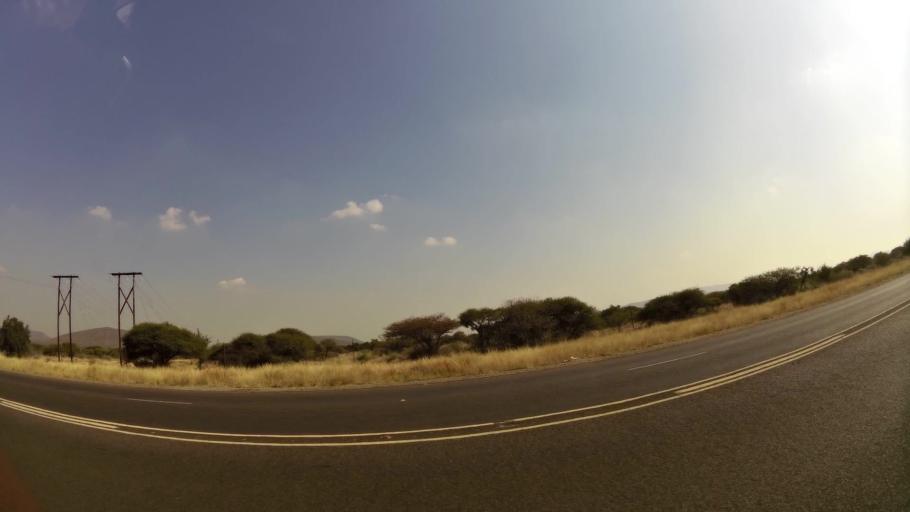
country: ZA
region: North-West
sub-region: Bojanala Platinum District Municipality
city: Mogwase
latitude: -25.4142
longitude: 27.0773
